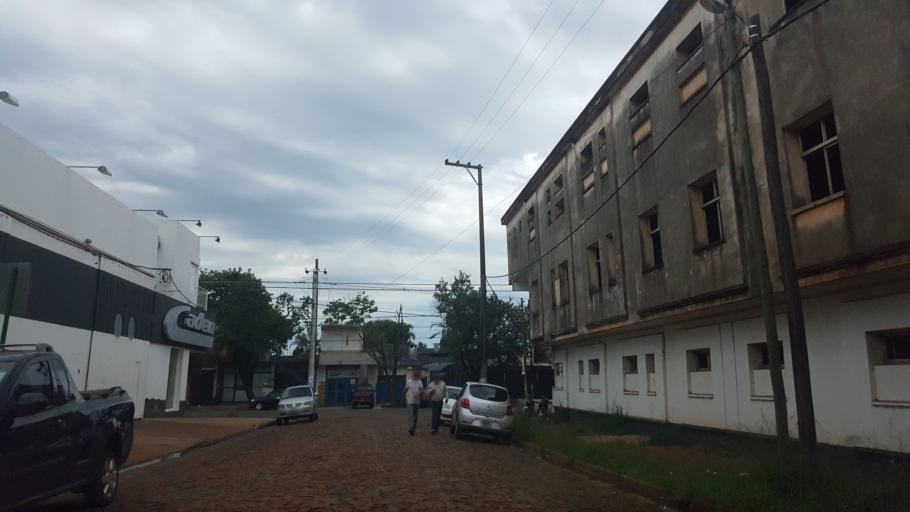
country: AR
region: Misiones
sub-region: Departamento de Capital
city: Posadas
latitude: -27.3984
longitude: -55.9100
